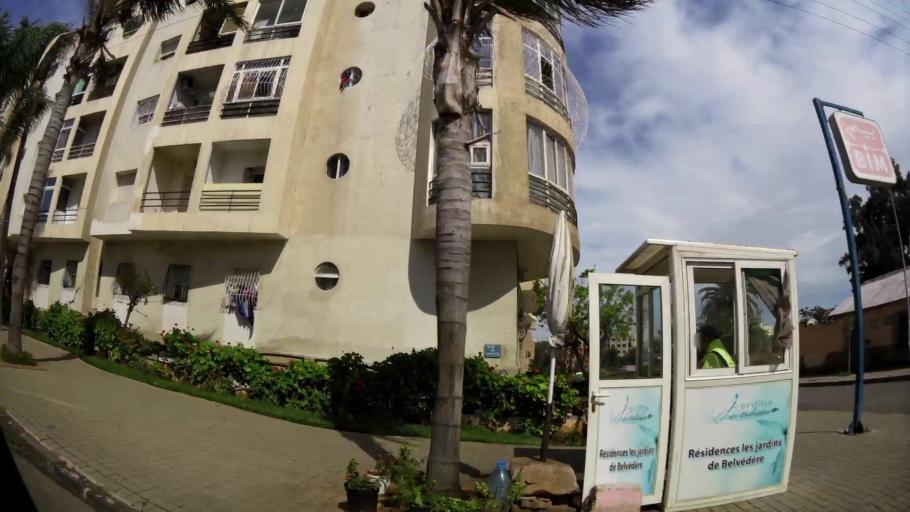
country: MA
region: Grand Casablanca
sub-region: Casablanca
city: Casablanca
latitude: 33.5849
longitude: -7.5892
